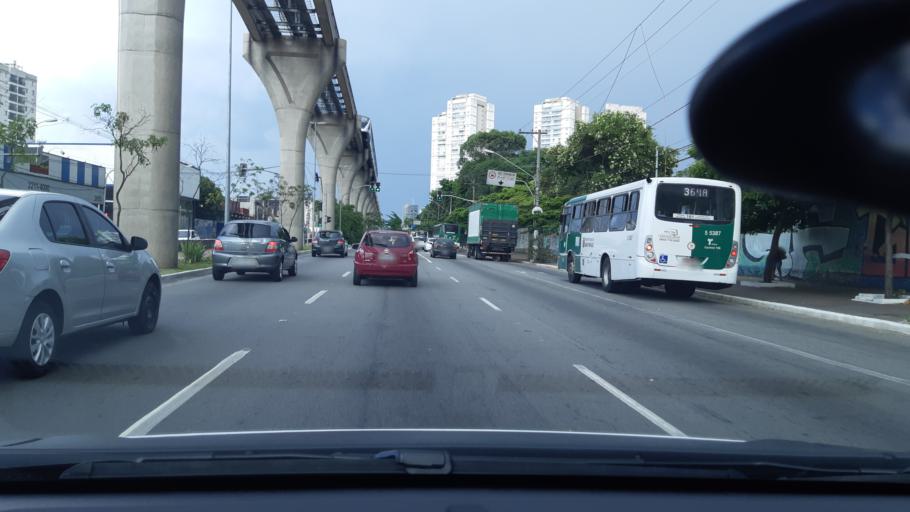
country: BR
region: Sao Paulo
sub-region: Sao Caetano Do Sul
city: Sao Caetano do Sul
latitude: -23.5830
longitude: -46.5682
